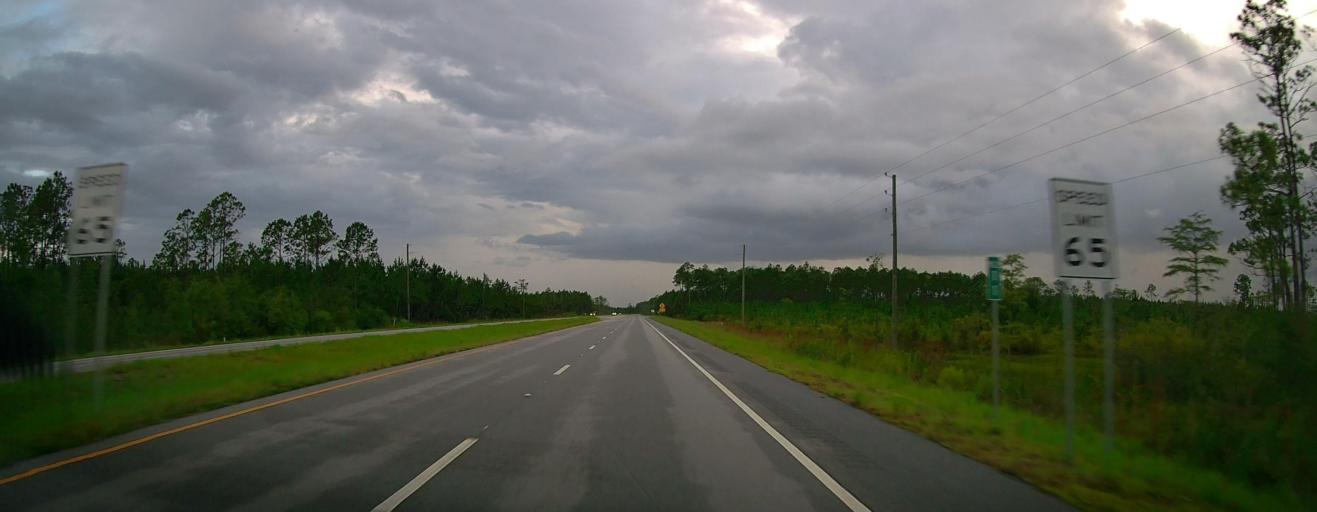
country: US
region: Georgia
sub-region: Ware County
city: Deenwood
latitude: 31.1510
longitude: -82.4574
